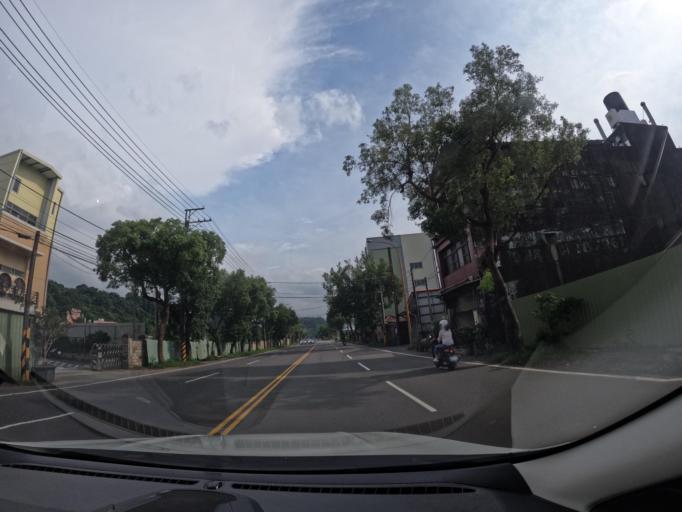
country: TW
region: Taiwan
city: Daxi
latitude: 24.8944
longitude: 121.3006
